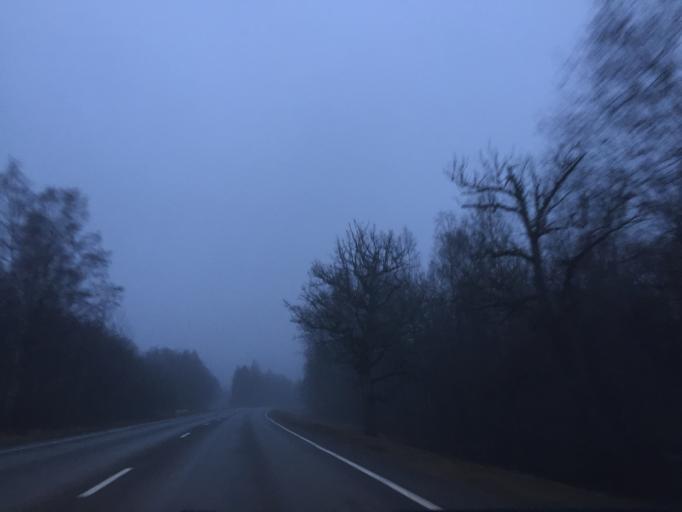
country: EE
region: Laeaene
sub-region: Lihula vald
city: Lihula
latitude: 58.6336
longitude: 23.6877
